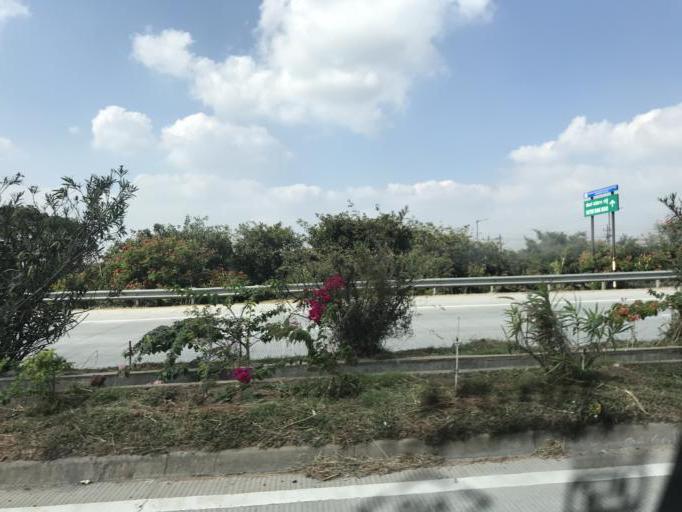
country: IN
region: Karnataka
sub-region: Bangalore Urban
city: Bangalore
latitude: 12.8838
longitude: 77.5012
